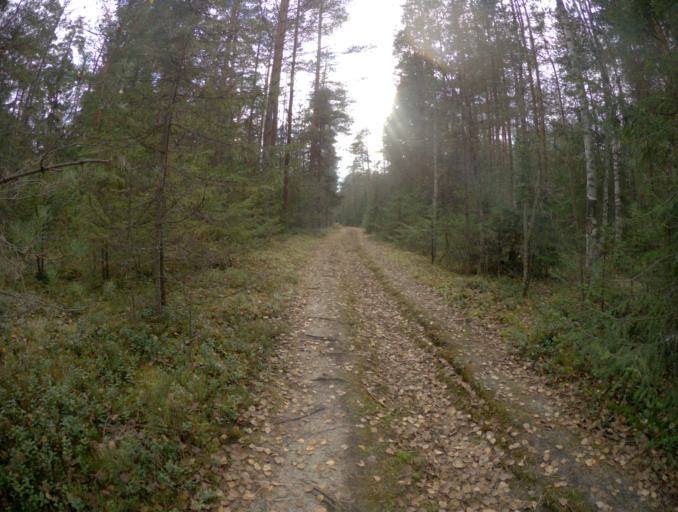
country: RU
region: Vladimir
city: Bogolyubovo
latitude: 56.0971
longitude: 40.5466
